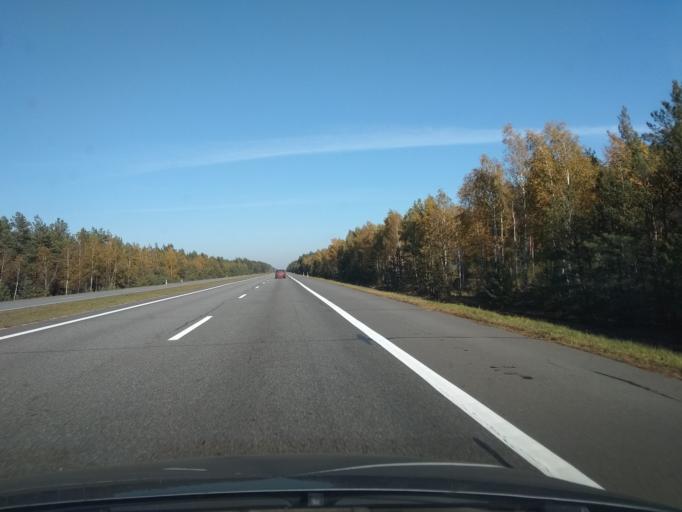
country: BY
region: Grodnenskaya
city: Zhyrovichy
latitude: 52.9271
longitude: 25.6933
